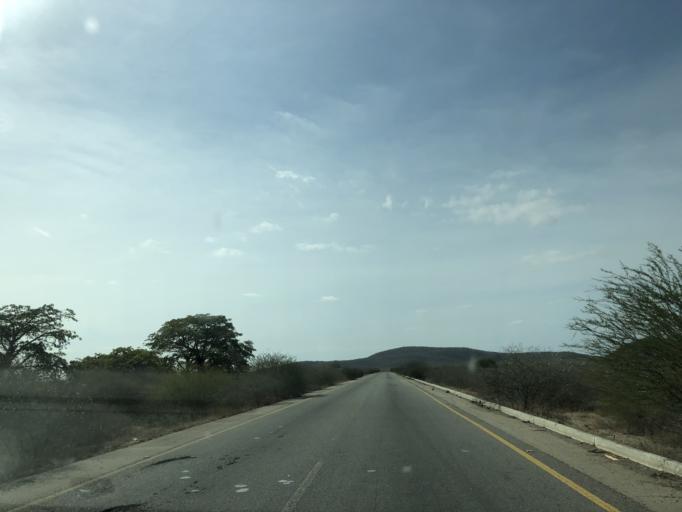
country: AO
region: Benguela
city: Benguela
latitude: -12.9048
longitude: 13.5047
